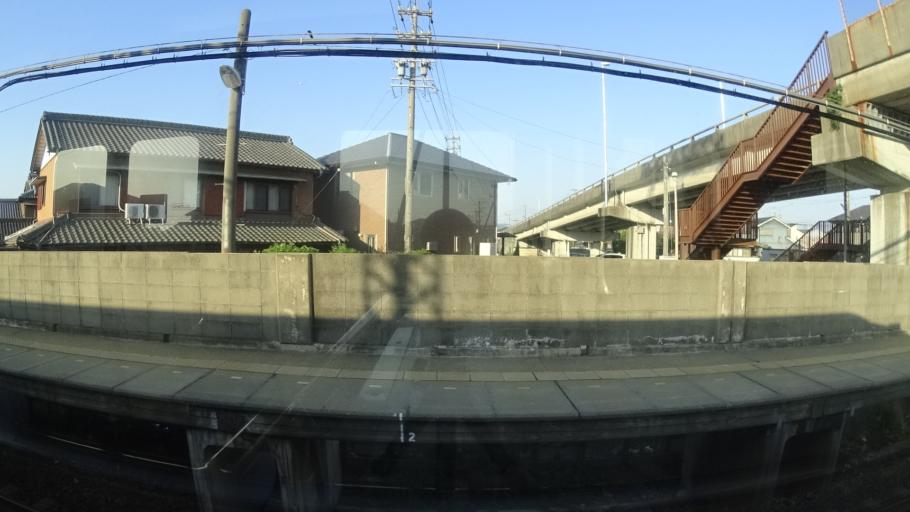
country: JP
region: Mie
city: Ise
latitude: 34.5131
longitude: 136.6844
